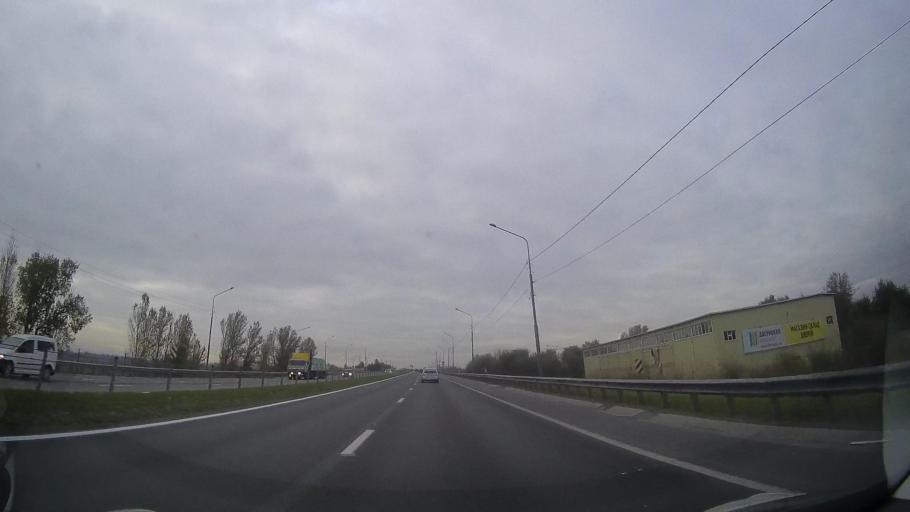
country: RU
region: Rostov
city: Bataysk
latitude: 47.1066
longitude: 39.7645
